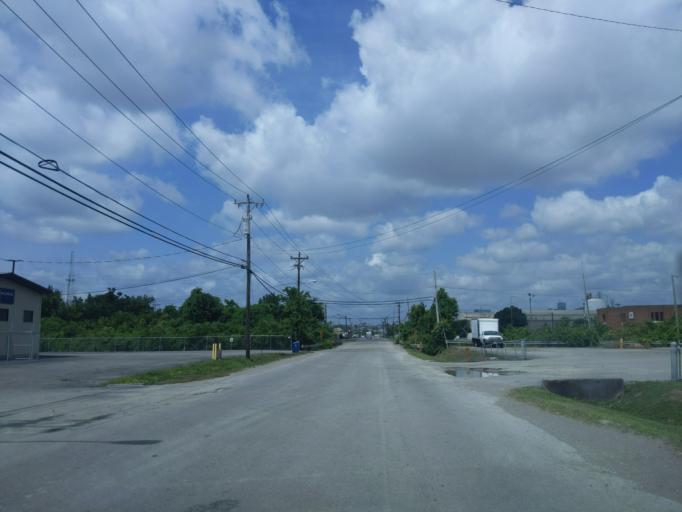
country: US
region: Tennessee
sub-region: Davidson County
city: Nashville
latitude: 36.1586
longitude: -86.7423
